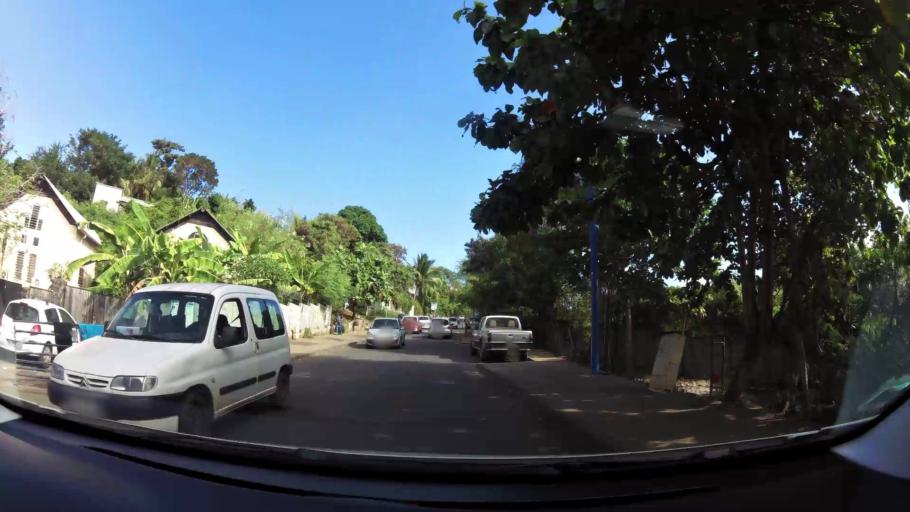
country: YT
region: Mamoudzou
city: Mamoudzou
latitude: -12.7844
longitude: 45.2229
